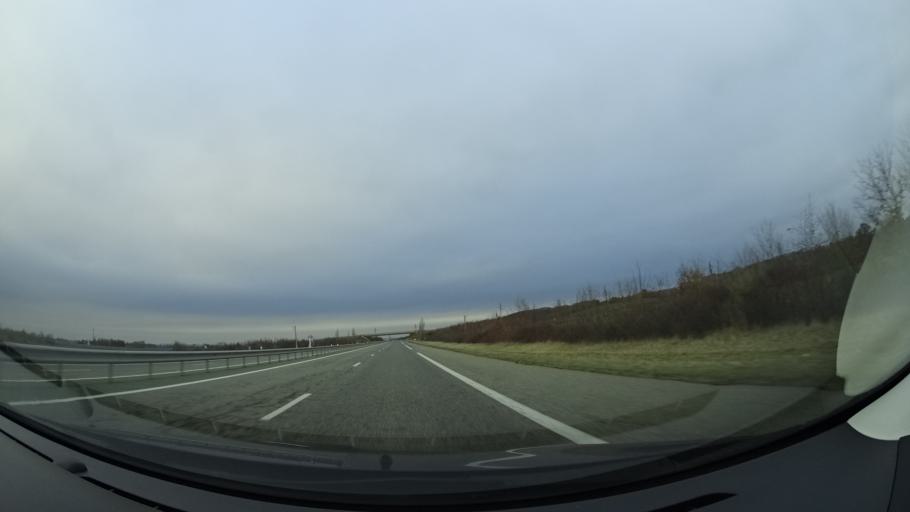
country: FR
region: Midi-Pyrenees
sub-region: Departement de l'Ariege
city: Saverdun
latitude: 43.1952
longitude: 1.6298
